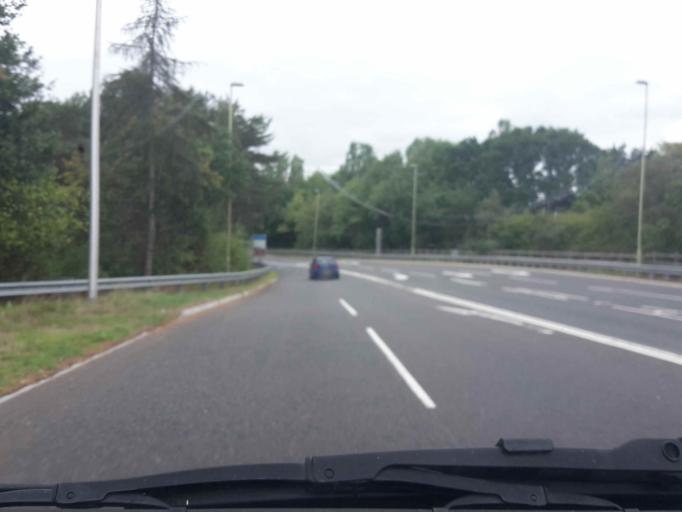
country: GB
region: England
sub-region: Hampshire
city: Fleet
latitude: 51.2941
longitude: -0.8036
